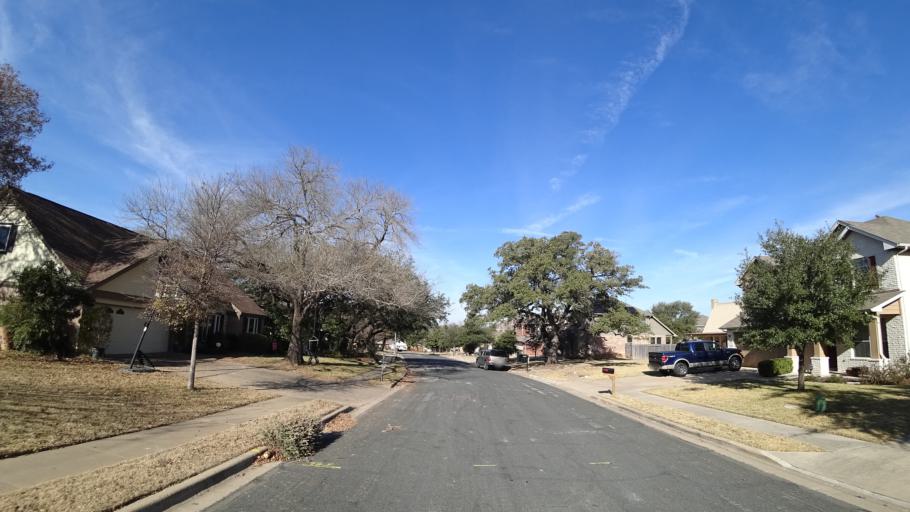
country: US
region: Texas
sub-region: Travis County
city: Wells Branch
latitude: 30.3904
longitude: -97.6948
